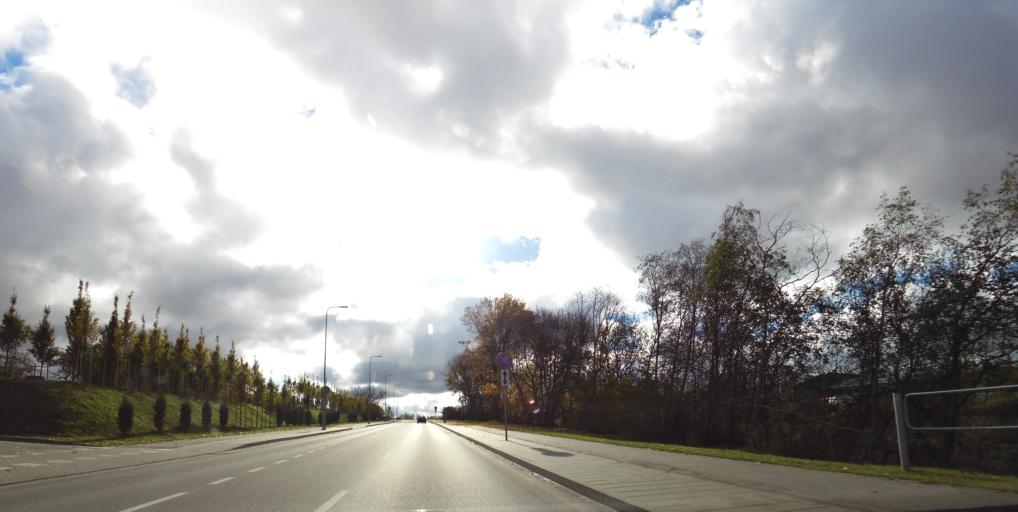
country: LT
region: Vilnius County
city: Naujamiestis
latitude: 54.6490
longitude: 25.2763
